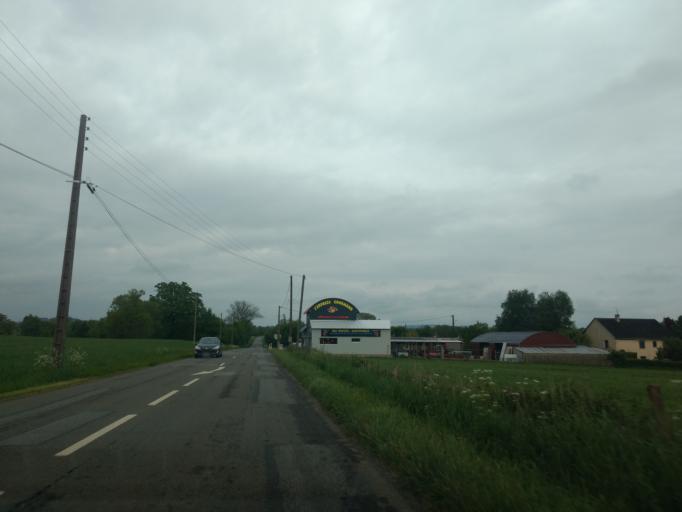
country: FR
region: Midi-Pyrenees
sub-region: Departement de l'Aveyron
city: Montbazens
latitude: 44.4583
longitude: 2.2338
